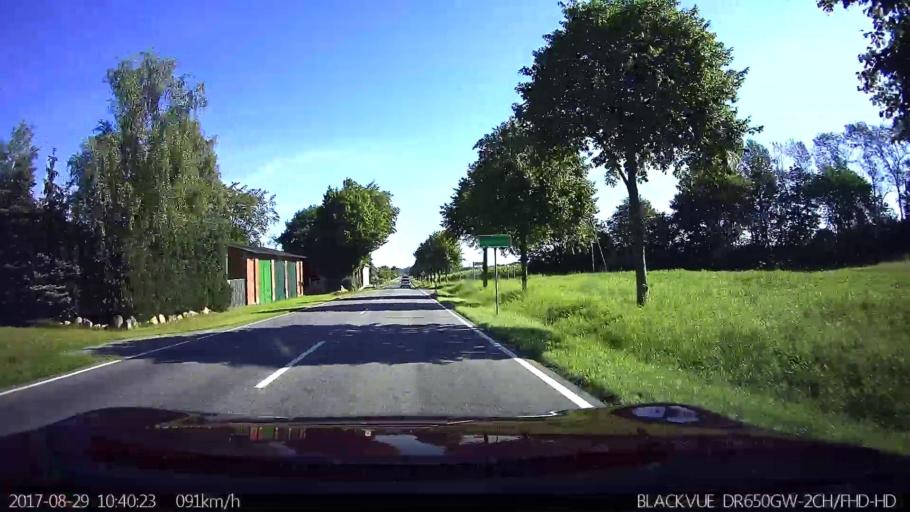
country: DE
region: Mecklenburg-Vorpommern
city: Franzburg
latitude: 54.1833
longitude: 12.8513
